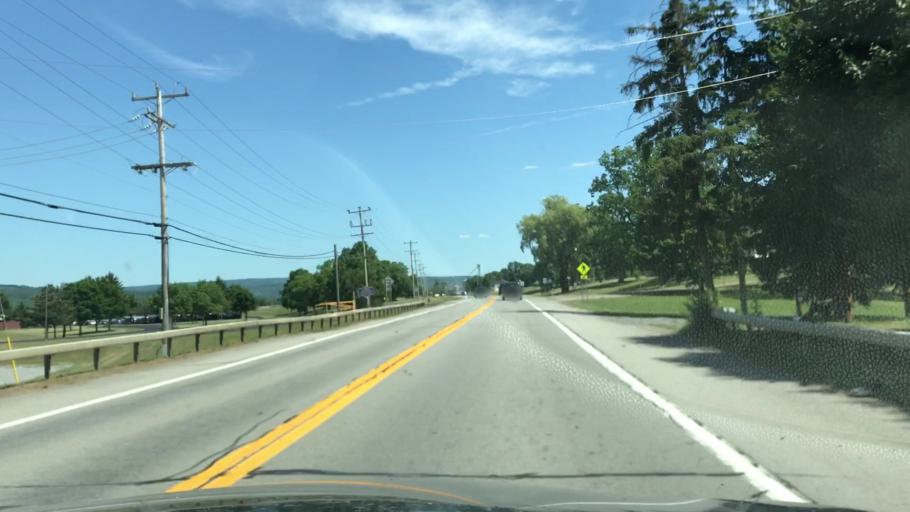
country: US
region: New York
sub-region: Livingston County
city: Mount Morris
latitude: 42.6830
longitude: -77.8280
